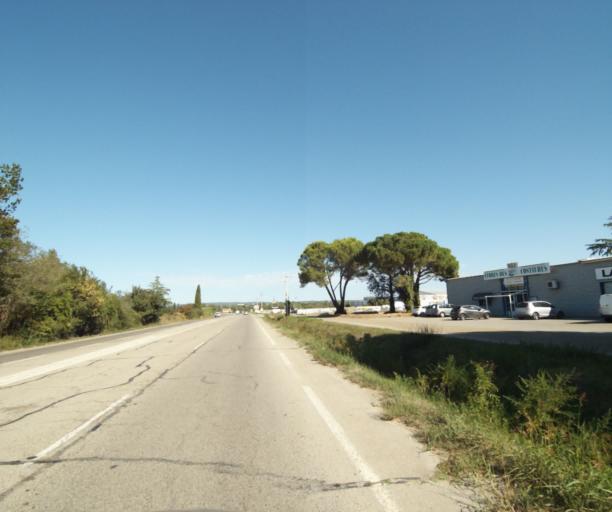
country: FR
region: Languedoc-Roussillon
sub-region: Departement du Gard
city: Caissargues
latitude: 43.8081
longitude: 4.4029
